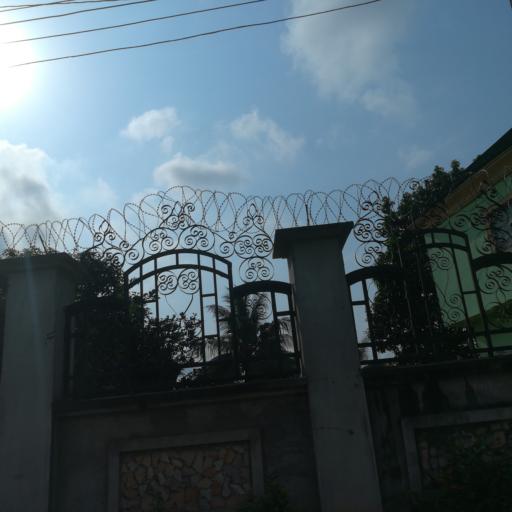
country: NG
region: Rivers
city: Okrika
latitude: 4.7781
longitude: 7.1335
